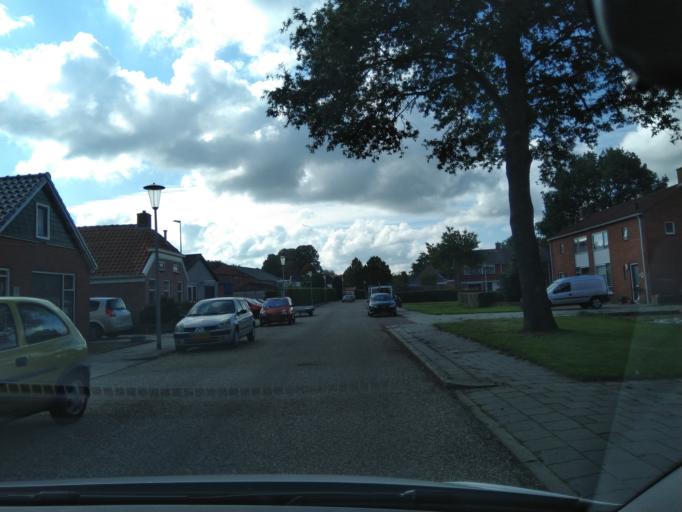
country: NL
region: Groningen
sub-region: Gemeente Veendam
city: Veendam
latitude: 53.0907
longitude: 6.9054
